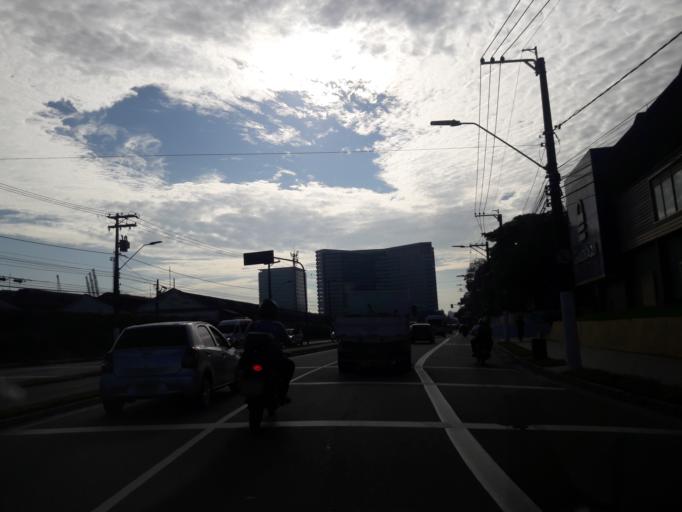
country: BR
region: Sao Paulo
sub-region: Santos
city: Santos
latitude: -23.9295
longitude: -46.3420
